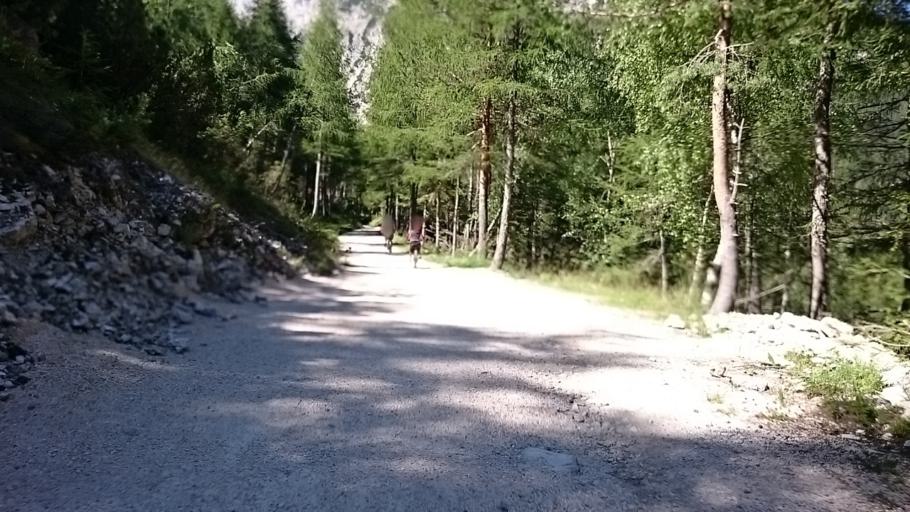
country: IT
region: Veneto
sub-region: Provincia di Belluno
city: Cortina d'Ampezzo
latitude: 46.5950
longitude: 12.1164
